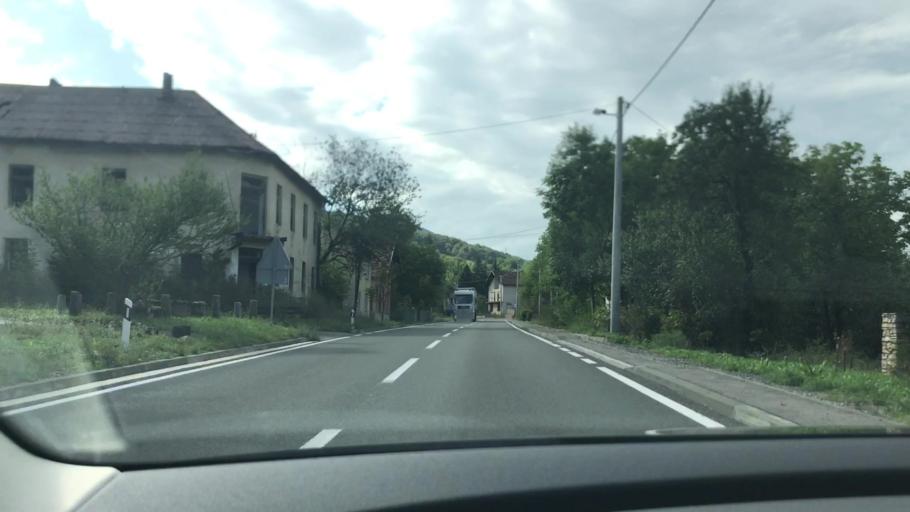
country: BA
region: Federation of Bosnia and Herzegovina
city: Izacic
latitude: 44.8804
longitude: 15.7106
